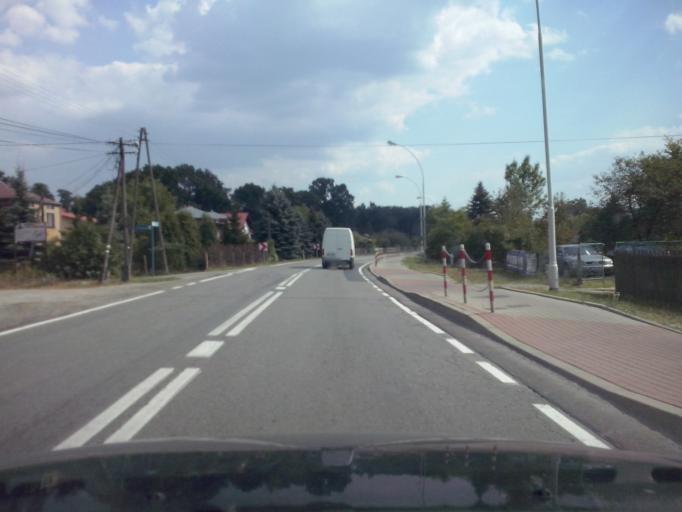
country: PL
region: Subcarpathian Voivodeship
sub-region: Powiat nizanski
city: Rudnik nad Sanem
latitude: 50.4307
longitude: 22.2699
